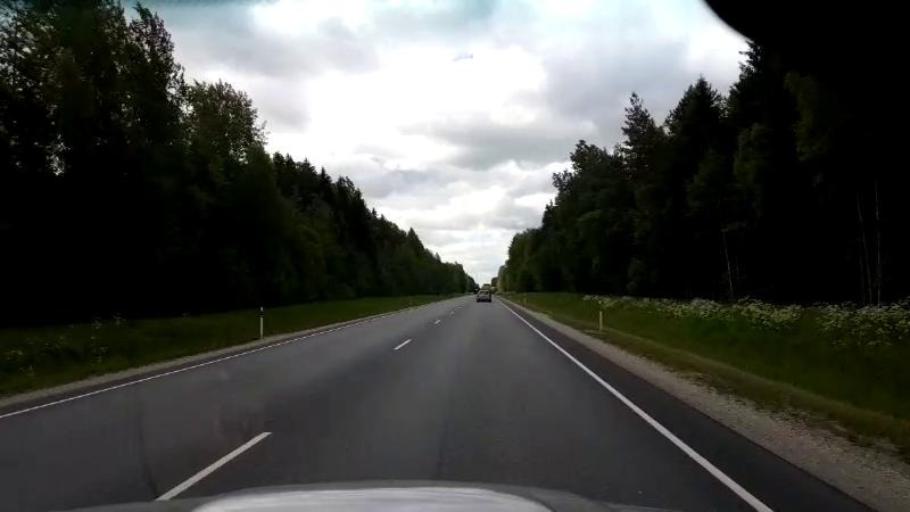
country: EE
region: Raplamaa
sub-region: Maerjamaa vald
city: Marjamaa
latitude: 58.7949
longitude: 24.4128
